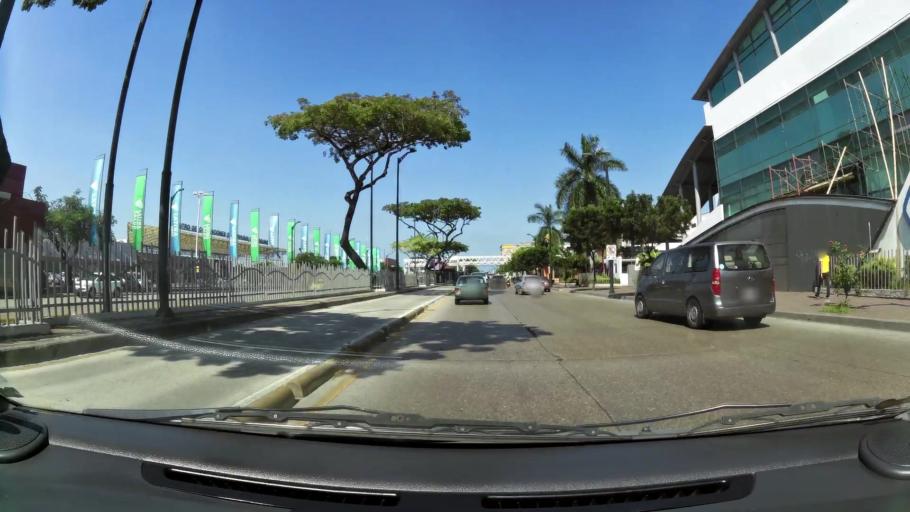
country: EC
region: Guayas
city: Eloy Alfaro
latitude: -2.1575
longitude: -79.8880
